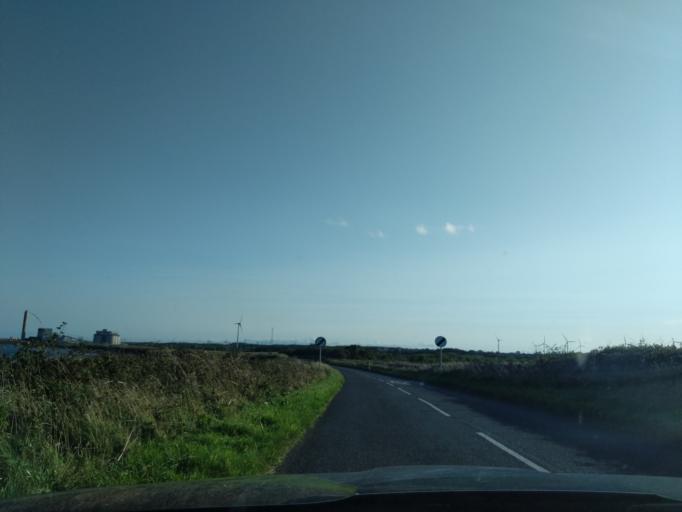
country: GB
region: England
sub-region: Northumberland
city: Lynemouth
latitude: 55.2240
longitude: -1.5293
